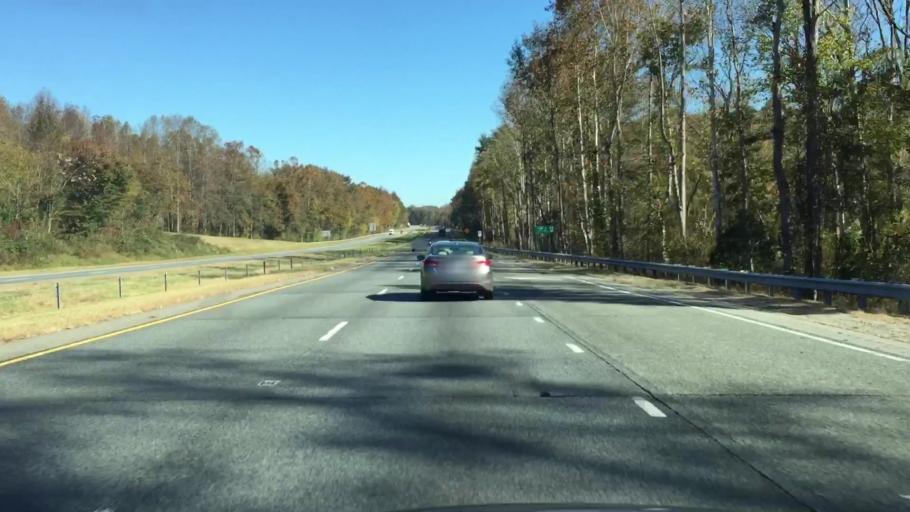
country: US
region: North Carolina
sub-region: Rockingham County
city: Reidsville
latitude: 36.2617
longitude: -79.6512
